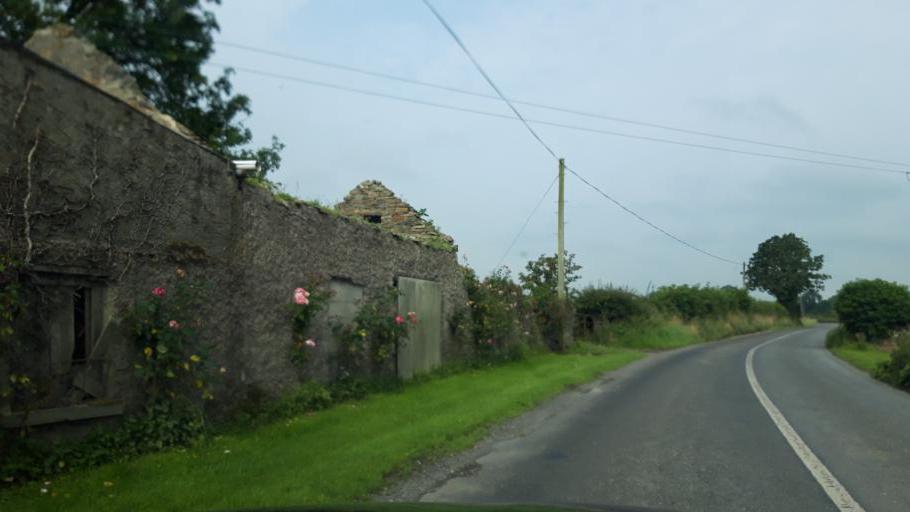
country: IE
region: Leinster
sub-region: Kilkenny
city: Callan
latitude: 52.5556
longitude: -7.5530
